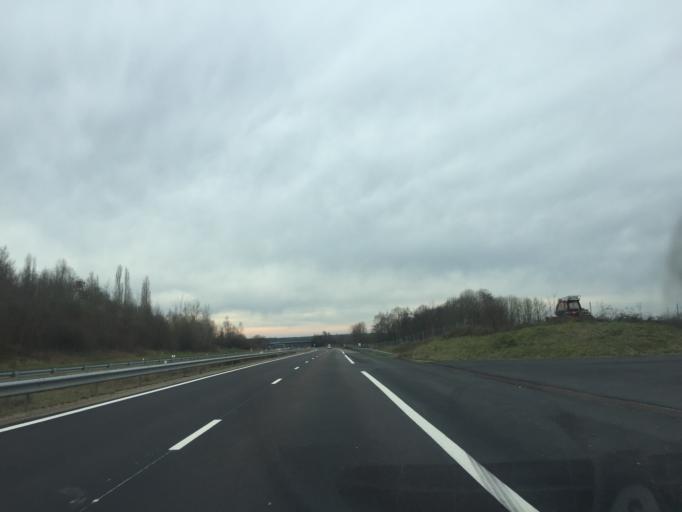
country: FR
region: Franche-Comte
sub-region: Departement du Jura
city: Bletterans
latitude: 46.8400
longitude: 5.5581
